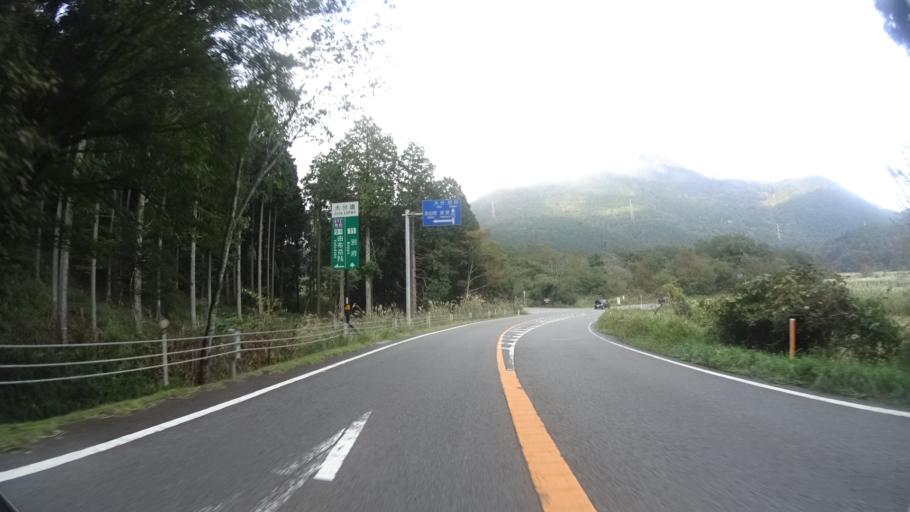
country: JP
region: Oita
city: Beppu
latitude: 33.2743
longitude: 131.4120
